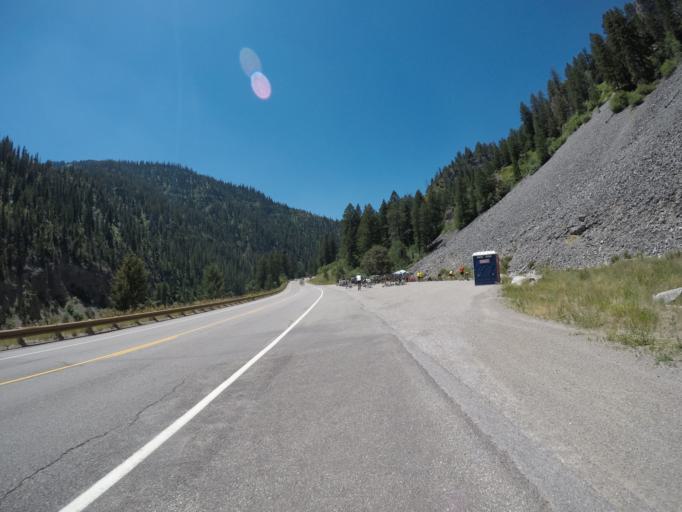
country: US
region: Wyoming
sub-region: Teton County
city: Hoback
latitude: 43.1975
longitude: -110.9083
